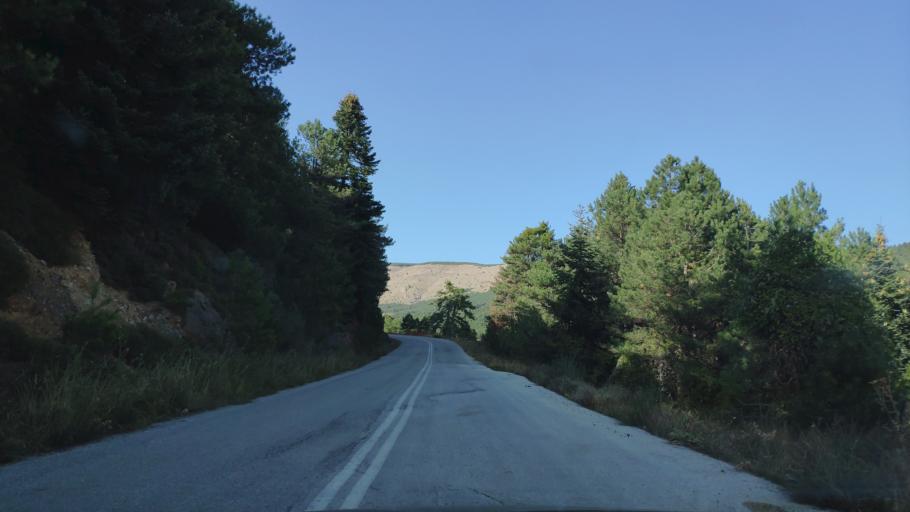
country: GR
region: West Greece
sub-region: Nomos Achaias
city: Aiyira
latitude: 38.0140
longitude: 22.4050
